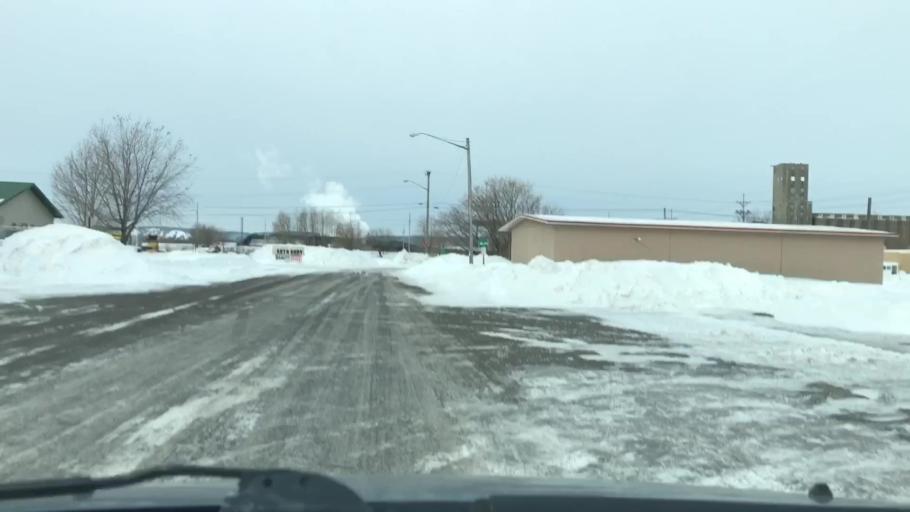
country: US
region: Wisconsin
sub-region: Douglas County
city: Superior
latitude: 46.7352
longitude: -92.1042
